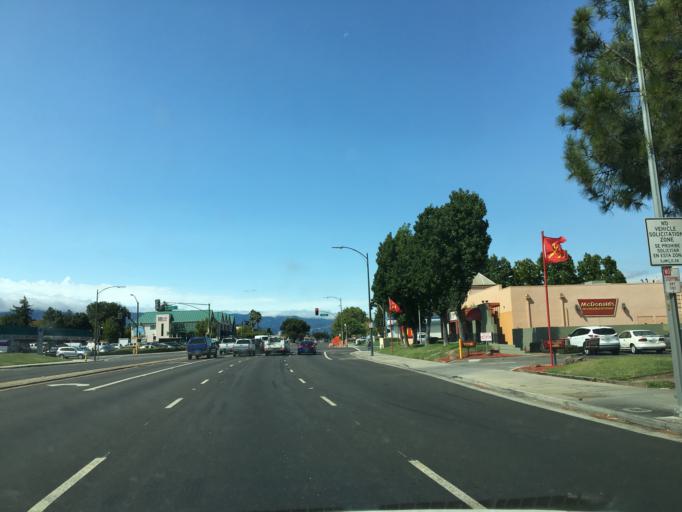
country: US
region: California
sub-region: Santa Clara County
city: Cambrian Park
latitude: 37.2619
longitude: -121.9212
